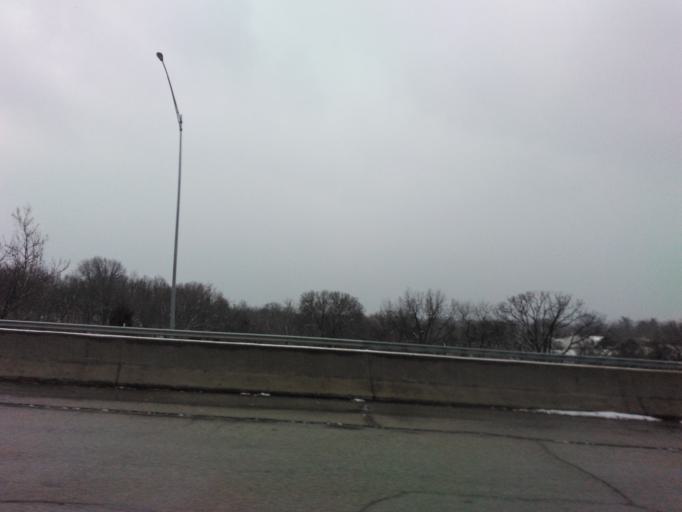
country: US
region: Missouri
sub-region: Saint Louis County
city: Green Park
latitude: 38.5055
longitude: -90.3449
